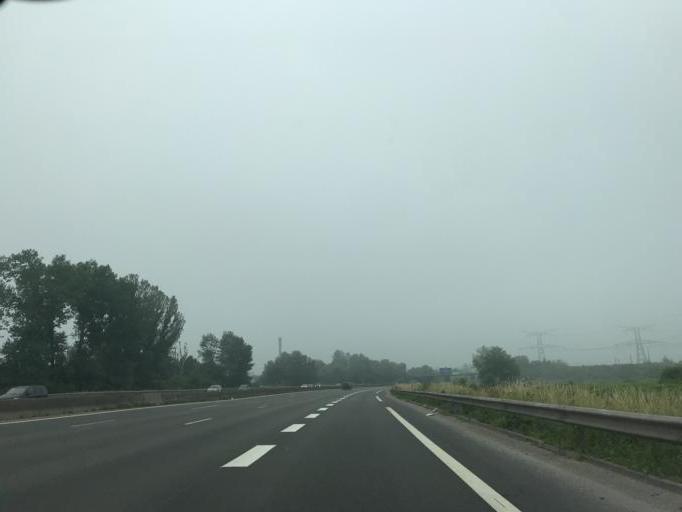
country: FR
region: Ile-de-France
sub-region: Departement de Seine-et-Marne
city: Saint-Thibault-des-Vignes
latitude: 48.8717
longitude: 2.6703
